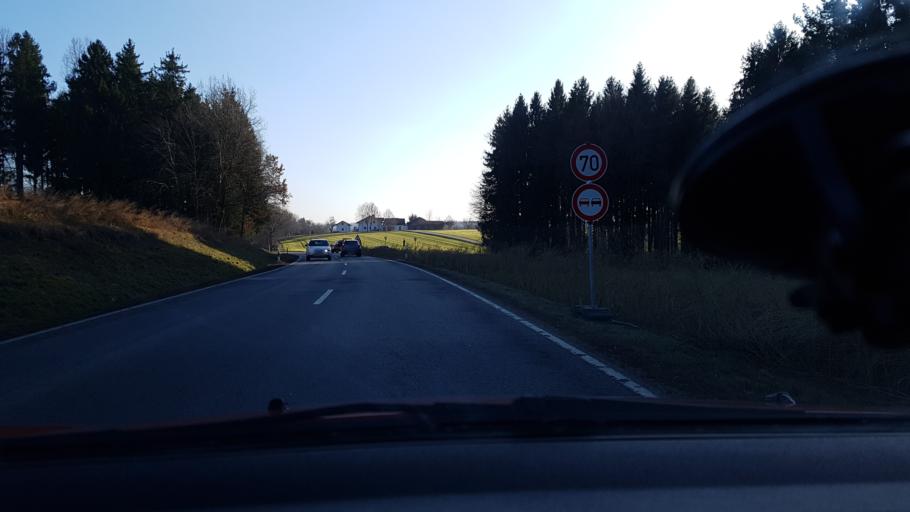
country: DE
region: Bavaria
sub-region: Lower Bavaria
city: Reut
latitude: 48.3144
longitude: 12.9522
